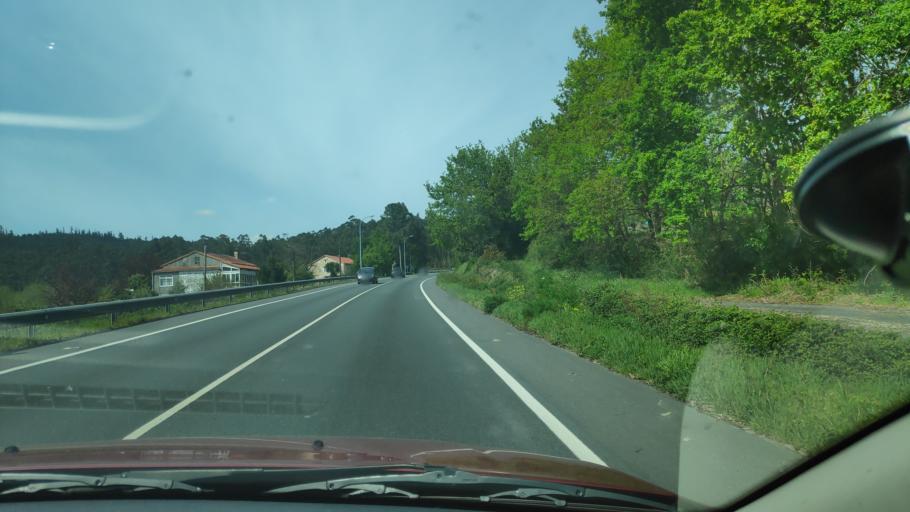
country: ES
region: Galicia
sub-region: Provincia da Coruna
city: Ames
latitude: 42.8712
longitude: -8.6587
